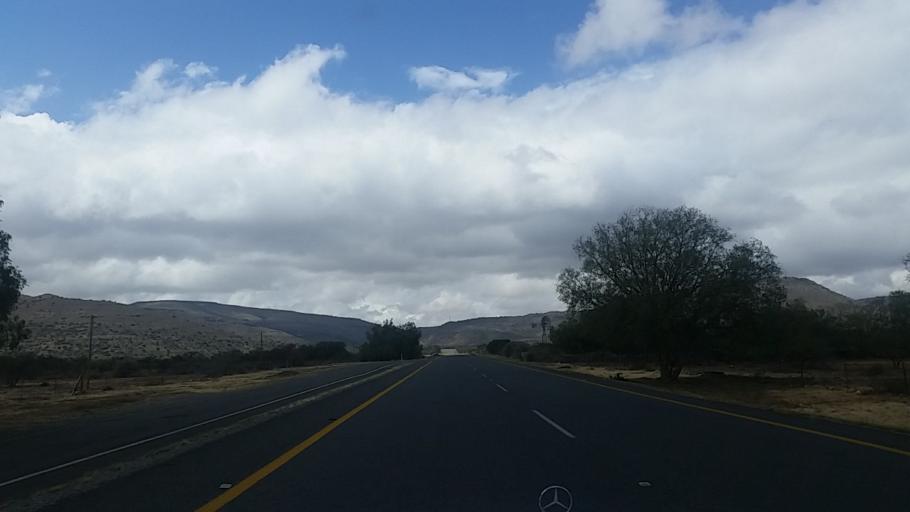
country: ZA
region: Eastern Cape
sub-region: Cacadu District Municipality
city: Graaff-Reinet
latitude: -31.9877
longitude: 24.6887
